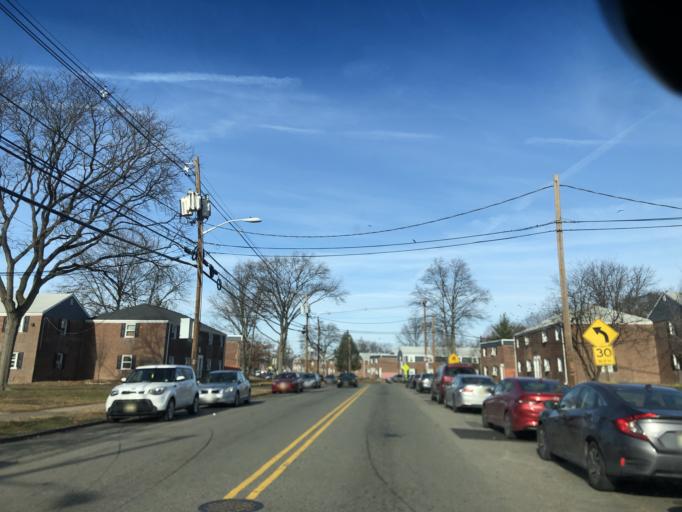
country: US
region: New Jersey
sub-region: Bergen County
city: Elmwood Park
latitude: 40.9154
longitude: -74.1230
